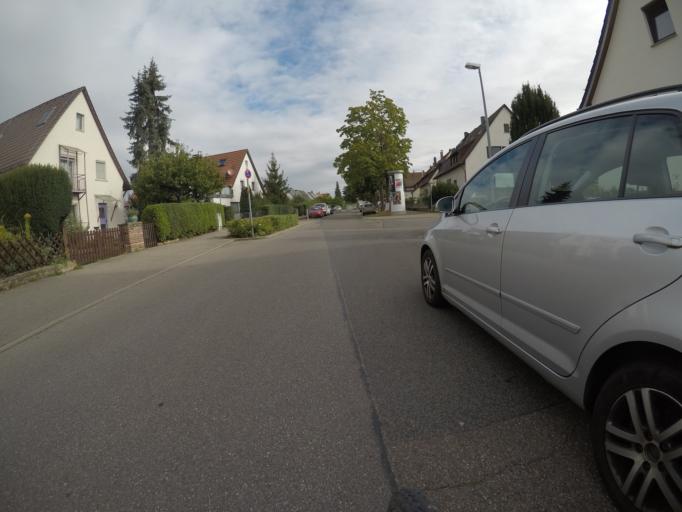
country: DE
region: Baden-Wuerttemberg
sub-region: Regierungsbezirk Stuttgart
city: Stuttgart Muehlhausen
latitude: 48.8333
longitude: 9.2194
